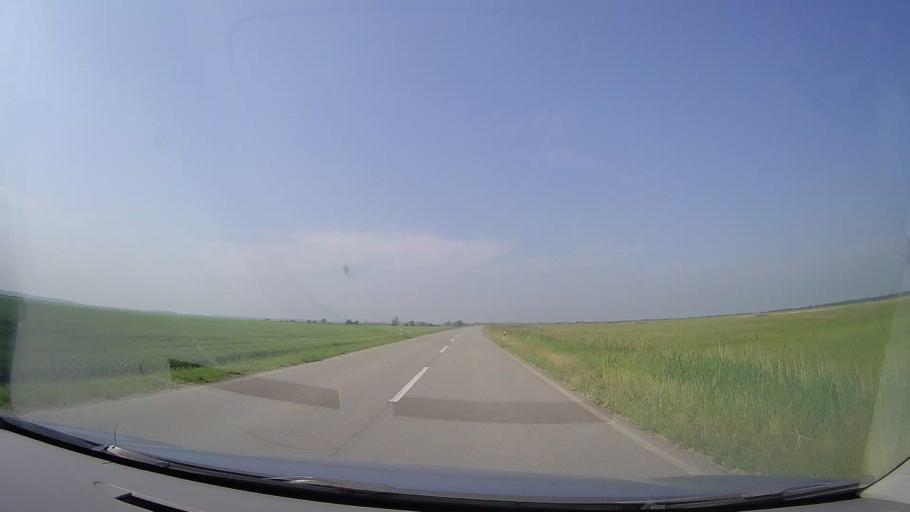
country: RS
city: Jasa Tomic
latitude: 45.4110
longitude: 20.8275
